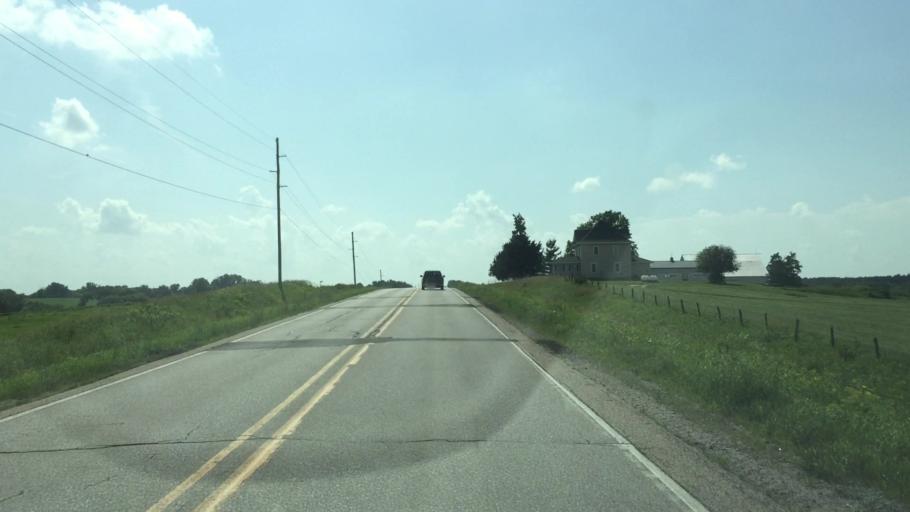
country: US
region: Iowa
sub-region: Linn County
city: Ely
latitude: 41.8475
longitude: -91.5897
